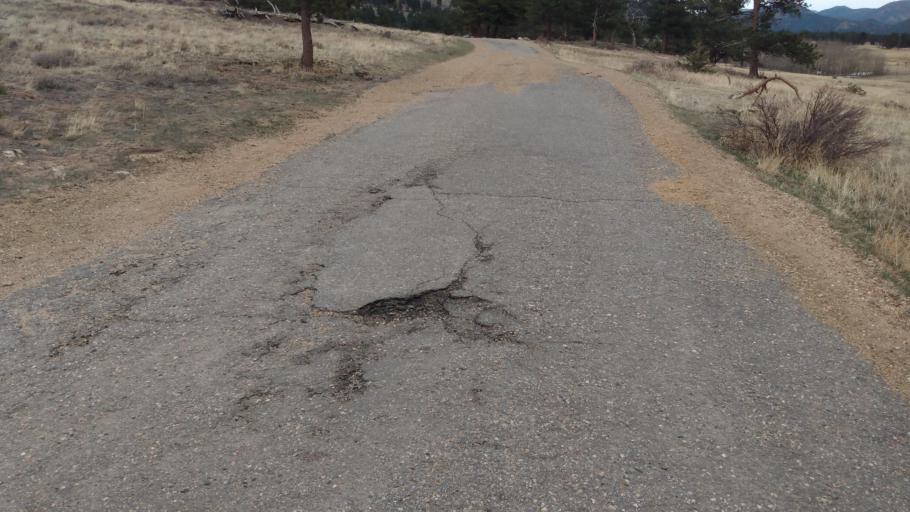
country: US
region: Colorado
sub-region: Larimer County
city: Estes Park
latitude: 40.3718
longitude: -105.6099
